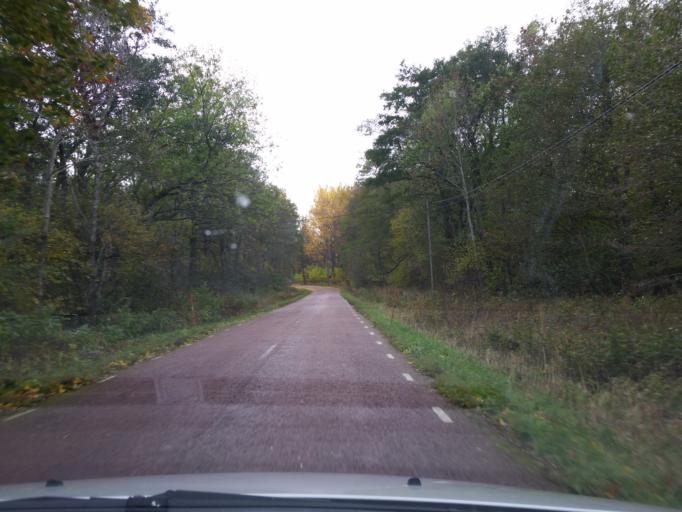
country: AX
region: Alands landsbygd
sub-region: Lemland
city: Lemland
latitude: 59.9768
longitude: 20.1837
